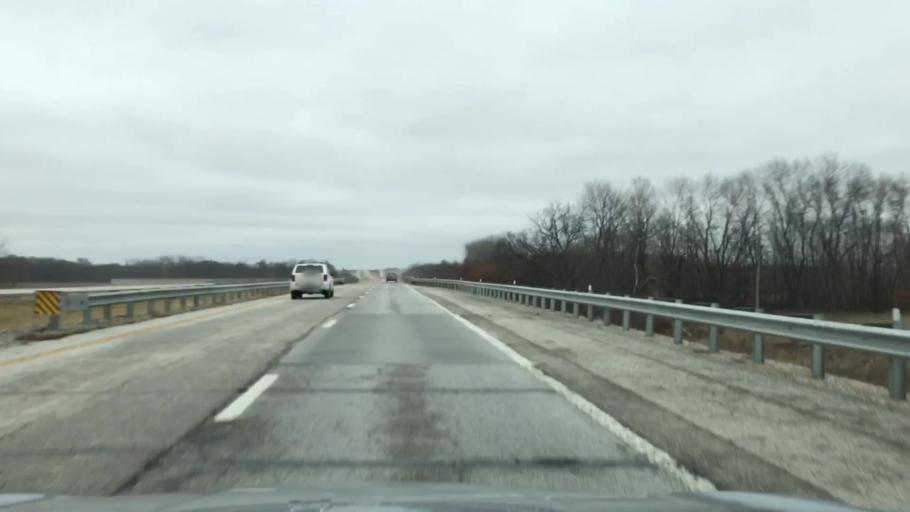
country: US
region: Missouri
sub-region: Linn County
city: Marceline
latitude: 39.7614
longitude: -92.9845
